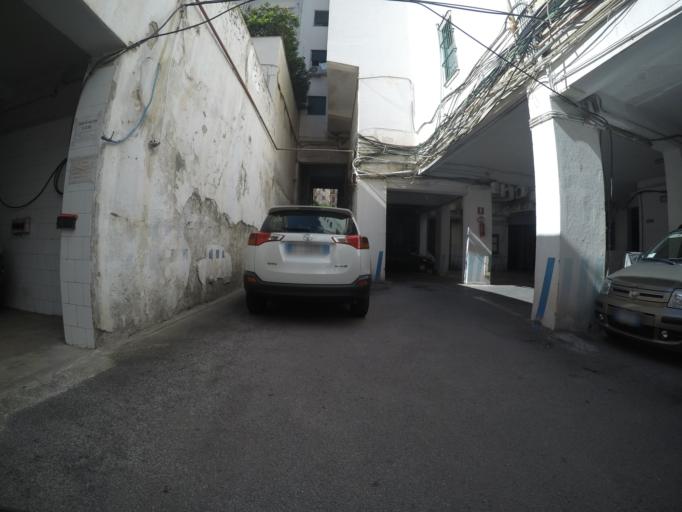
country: IT
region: Sicily
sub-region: Palermo
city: Palermo
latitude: 38.1347
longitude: 13.3552
